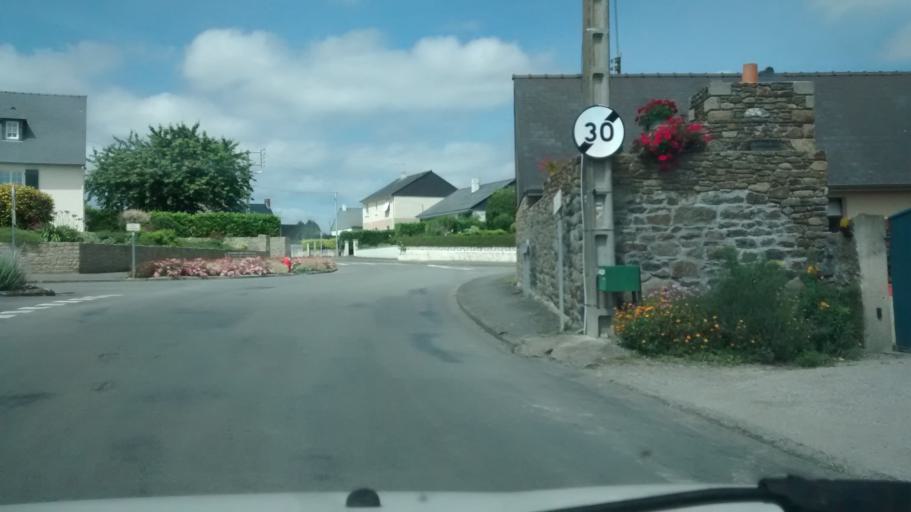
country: FR
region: Brittany
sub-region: Departement d'Ille-et-Vilaine
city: La Gouesniere
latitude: 48.6066
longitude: -1.8934
